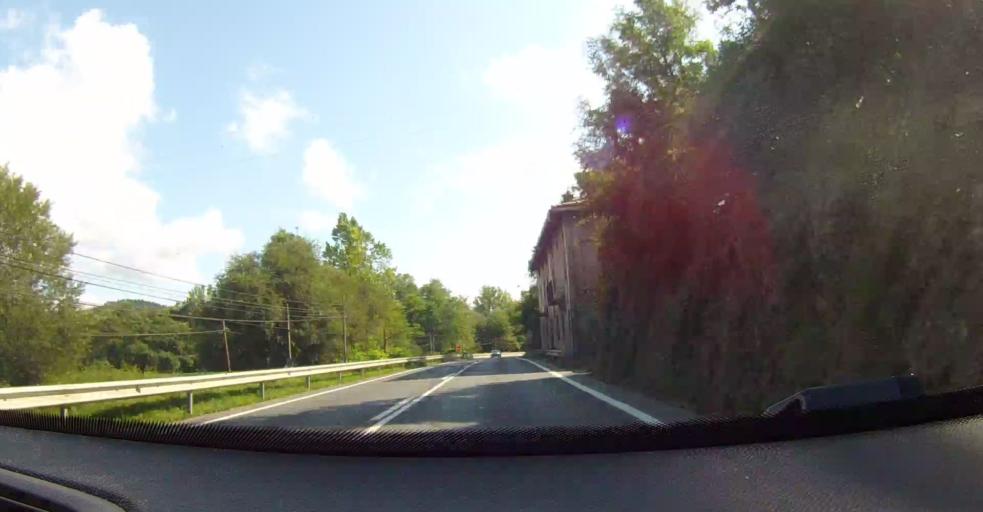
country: ES
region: Basque Country
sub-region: Bizkaia
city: Muxika
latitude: 43.2933
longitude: -2.6873
